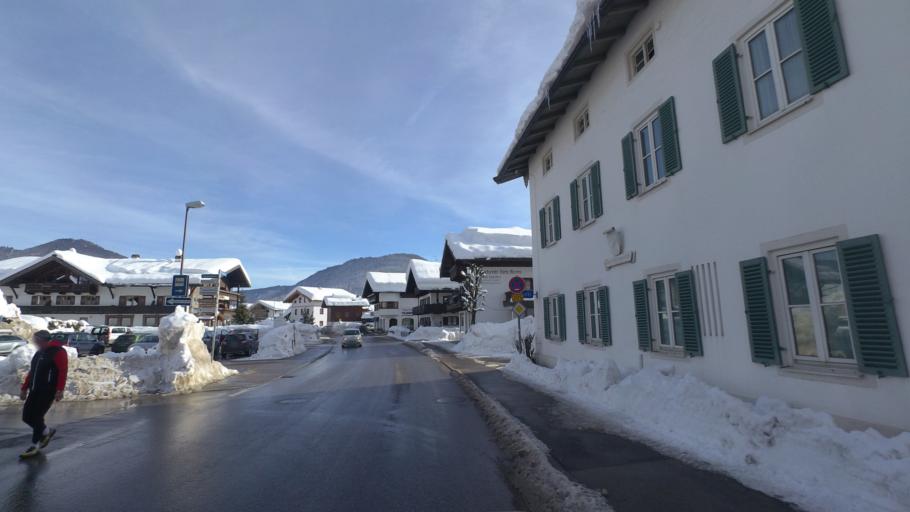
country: DE
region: Bavaria
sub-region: Upper Bavaria
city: Reit im Winkl
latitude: 47.6766
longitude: 12.4719
